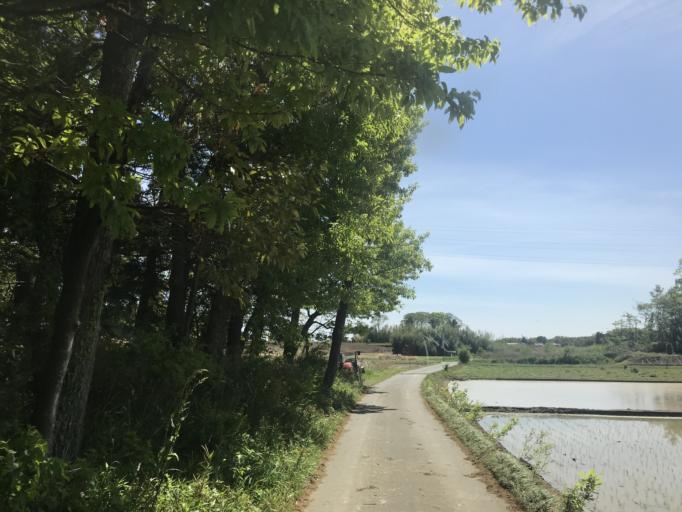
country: JP
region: Ibaraki
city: Mitsukaido
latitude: 36.0131
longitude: 139.9796
